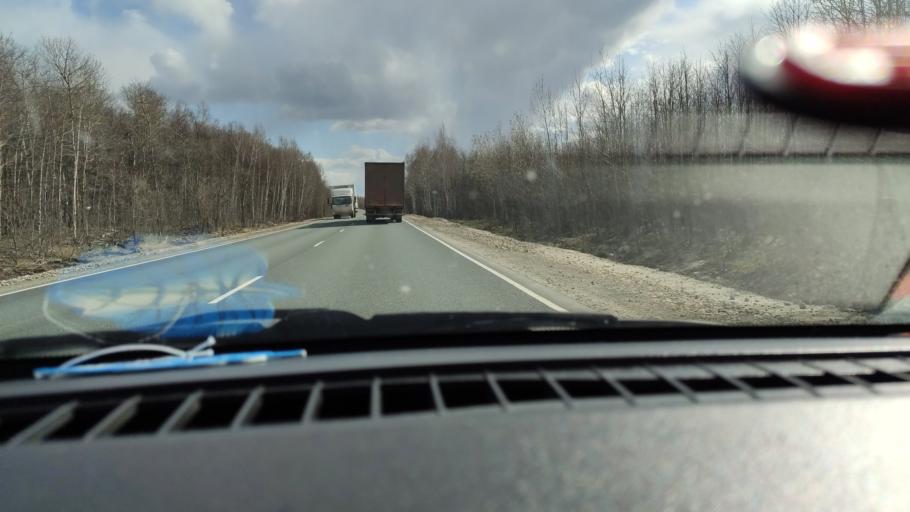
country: RU
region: Saratov
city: Khvalynsk
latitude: 52.4790
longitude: 48.0131
